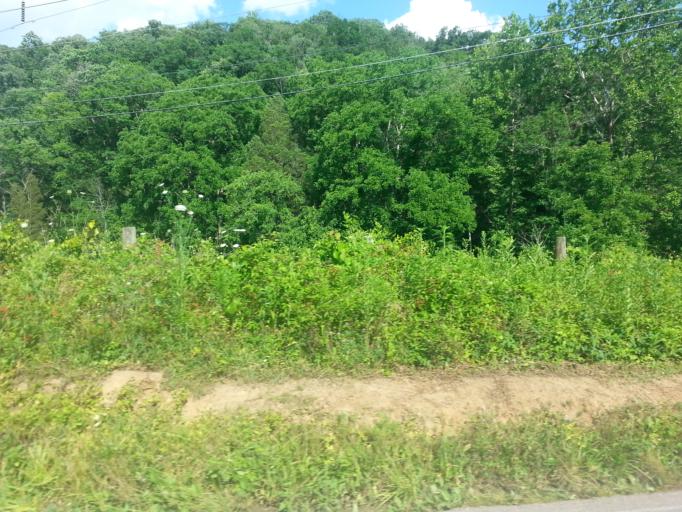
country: US
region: Tennessee
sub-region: Knox County
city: Knoxville
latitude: 36.0817
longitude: -83.8997
